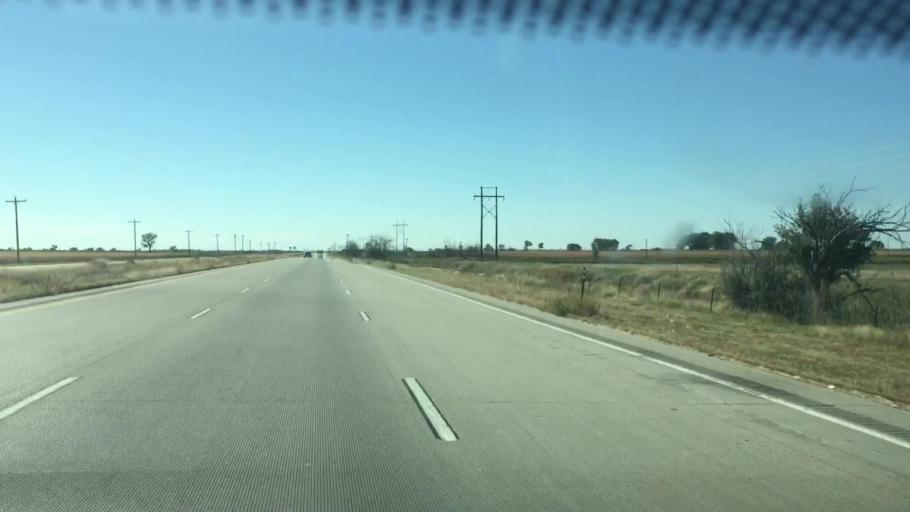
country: US
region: Colorado
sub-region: Prowers County
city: Lamar
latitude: 38.1105
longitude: -102.6735
